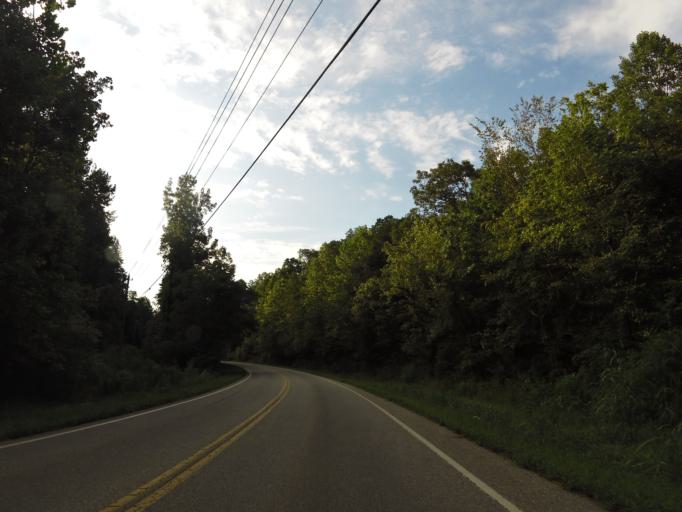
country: US
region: Tennessee
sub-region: Monroe County
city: Vonore
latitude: 35.6189
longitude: -84.3035
